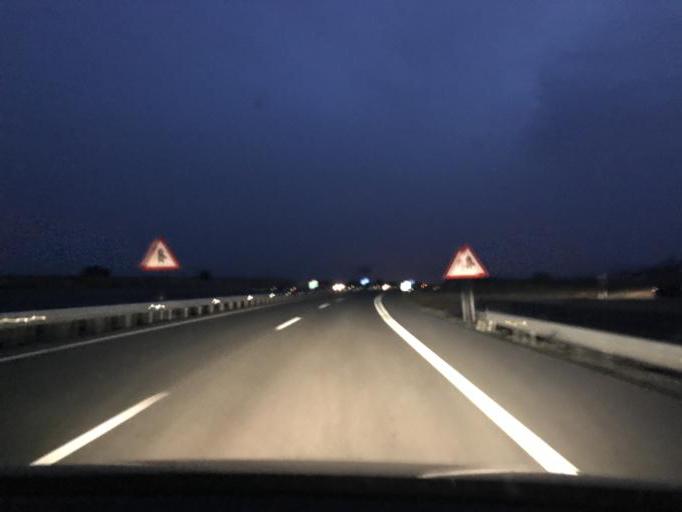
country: ES
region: Andalusia
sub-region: Provincia de Granada
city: Benalua de Guadix
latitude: 37.3677
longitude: -3.0724
